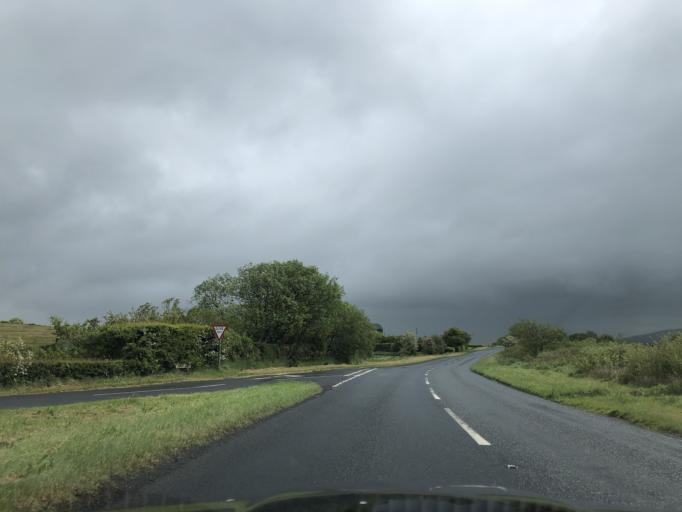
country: GB
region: Northern Ireland
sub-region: Moyle District
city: Ballycastle
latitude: 55.1690
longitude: -6.3562
